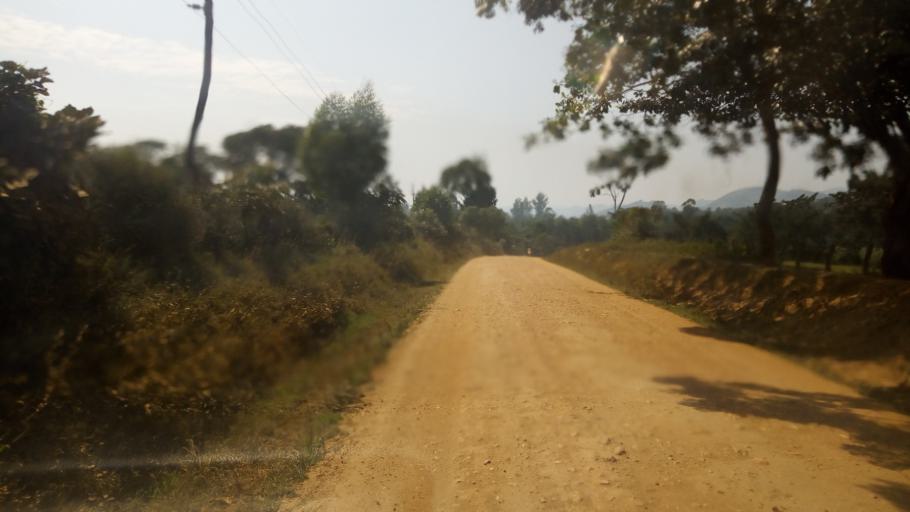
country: UG
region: Western Region
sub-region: Kanungu District
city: Ntungamo
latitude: -0.9126
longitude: 29.6216
